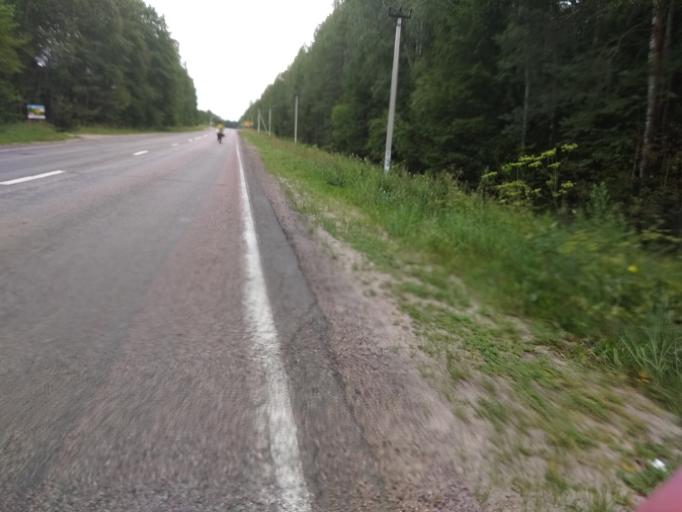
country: RU
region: Moskovskaya
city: Misheronskiy
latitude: 55.6156
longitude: 39.7228
